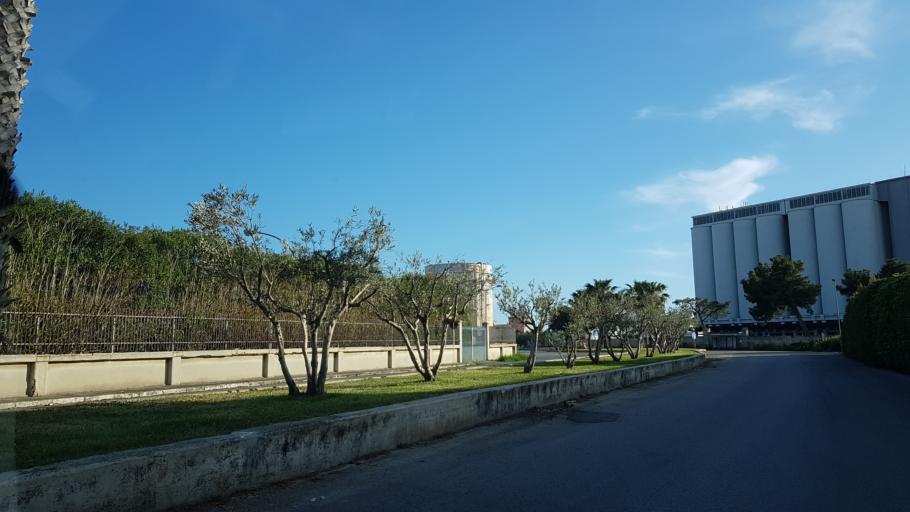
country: IT
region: Apulia
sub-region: Provincia di Brindisi
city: Materdomini
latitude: 40.6397
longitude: 17.9555
